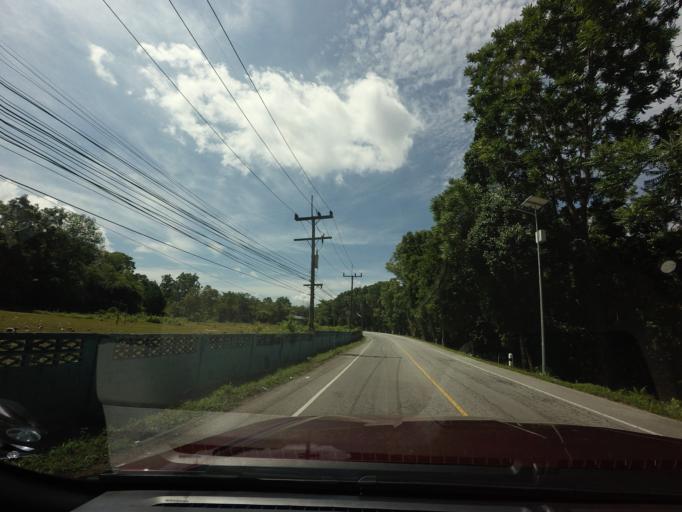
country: TH
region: Narathiwat
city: Rueso
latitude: 6.3836
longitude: 101.5156
